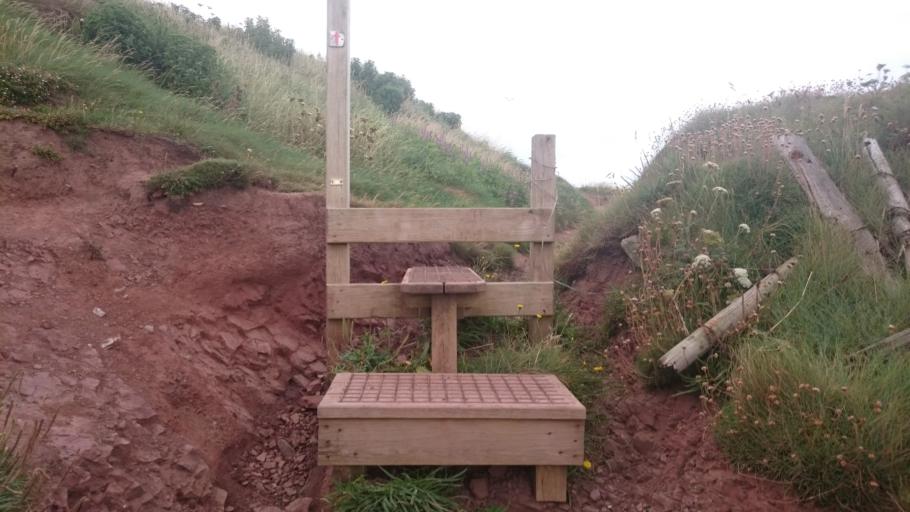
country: IE
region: Munster
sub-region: Waterford
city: Dunmore East
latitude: 52.1411
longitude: -7.0026
